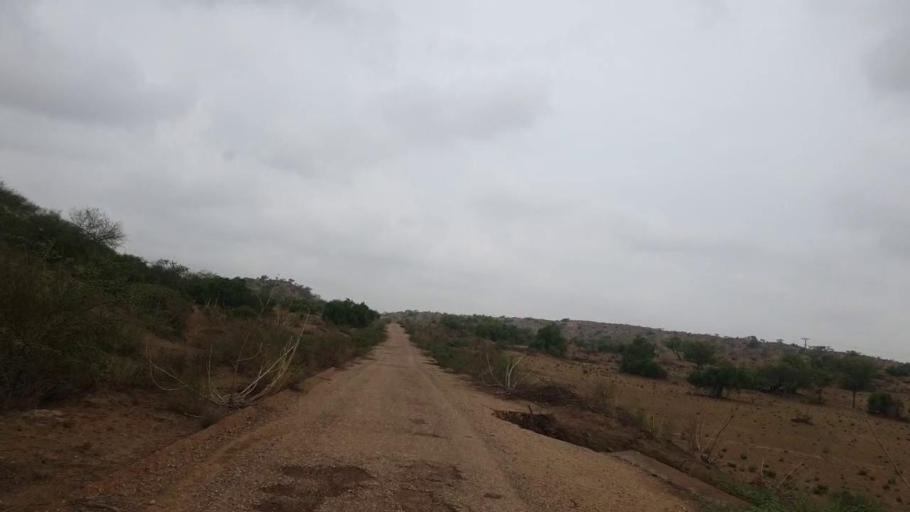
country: PK
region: Sindh
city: Diplo
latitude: 24.5131
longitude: 69.4952
